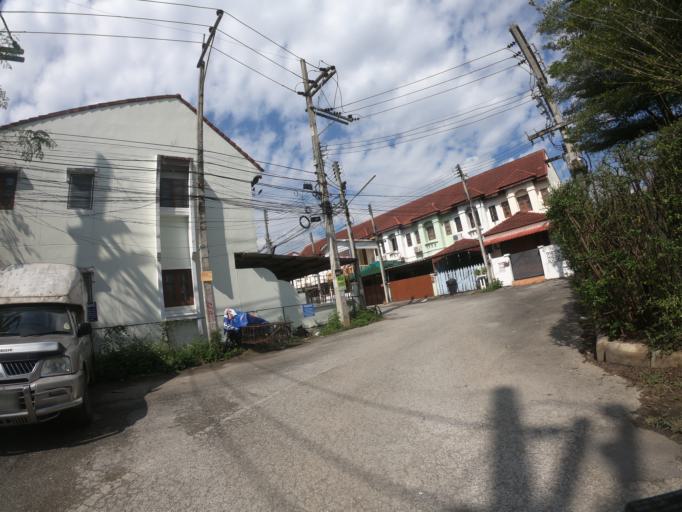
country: TH
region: Chiang Mai
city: Chiang Mai
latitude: 18.7375
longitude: 98.9608
